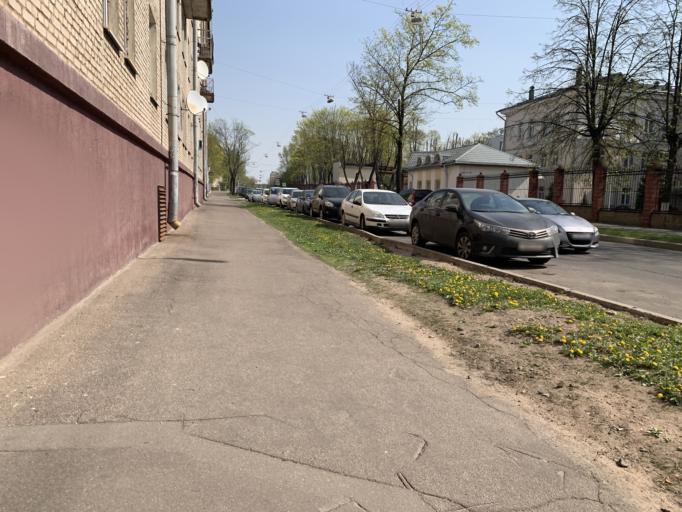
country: BY
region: Minsk
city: Minsk
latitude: 53.9100
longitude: 27.5816
